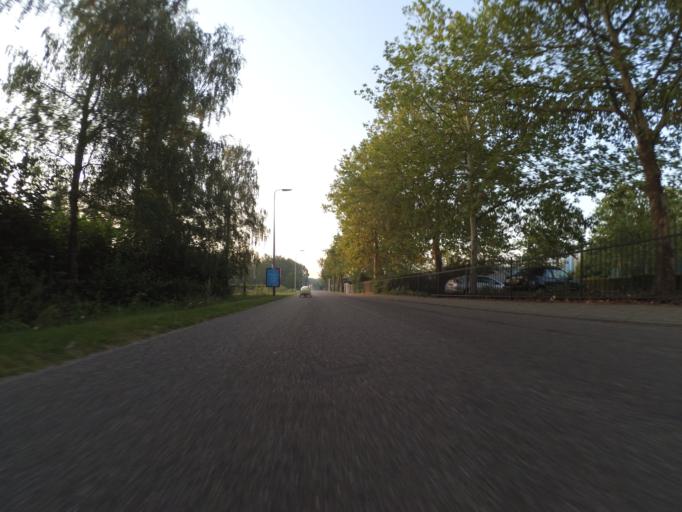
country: NL
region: Overijssel
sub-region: Gemeente Tubbergen
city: Tubbergen
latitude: 52.4052
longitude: 6.7888
